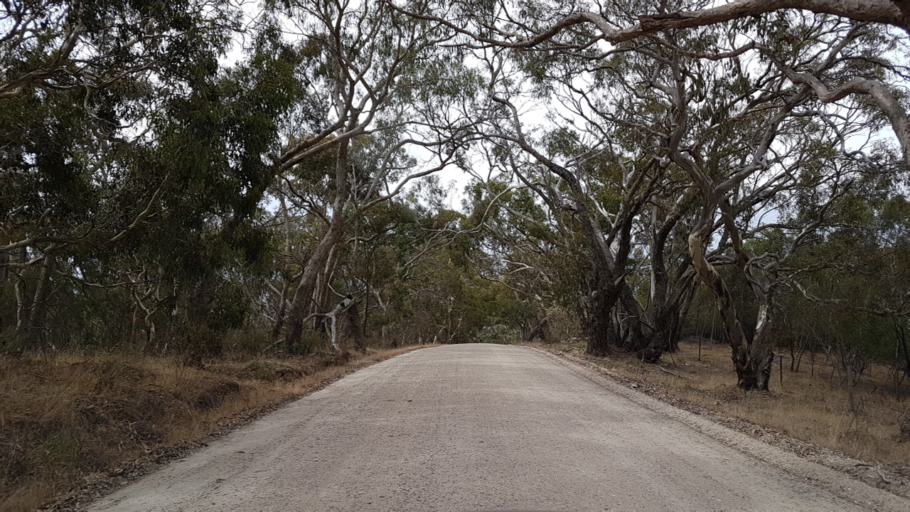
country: AU
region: South Australia
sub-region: Adelaide Hills
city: Birdwood
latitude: -34.7683
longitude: 138.9904
